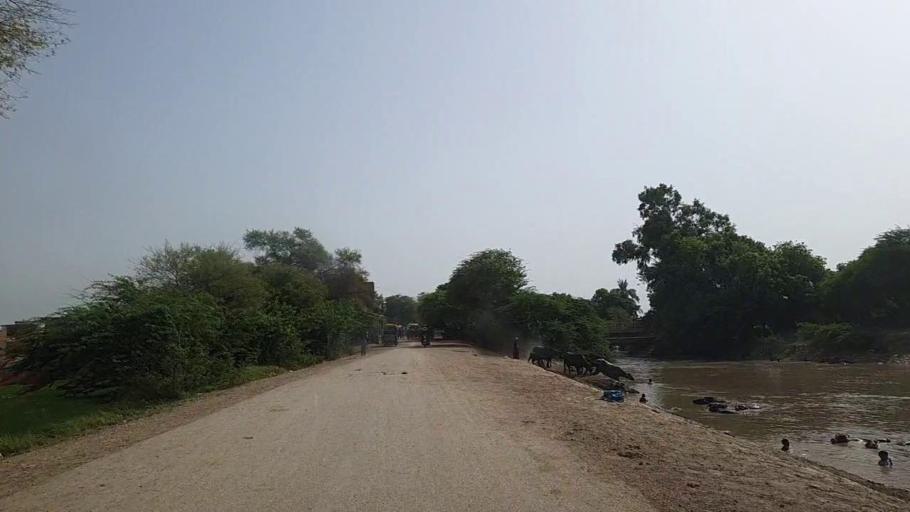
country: PK
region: Sindh
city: Mehar
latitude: 27.1277
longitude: 67.8650
